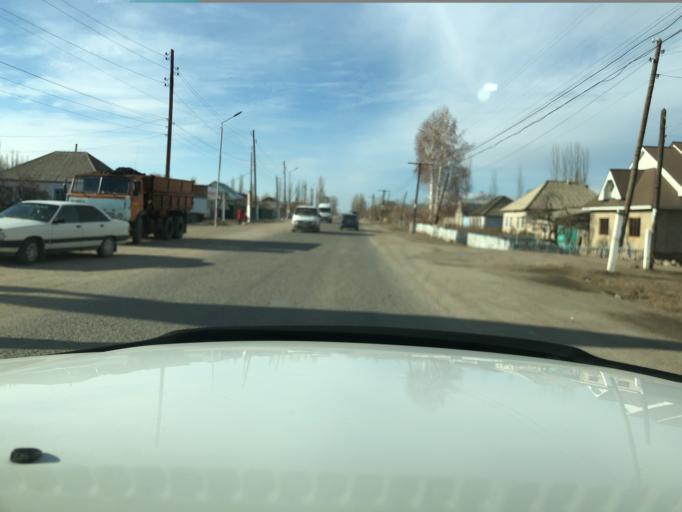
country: KG
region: Ysyk-Koel
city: Pokrovka
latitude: 42.3219
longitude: 77.9195
